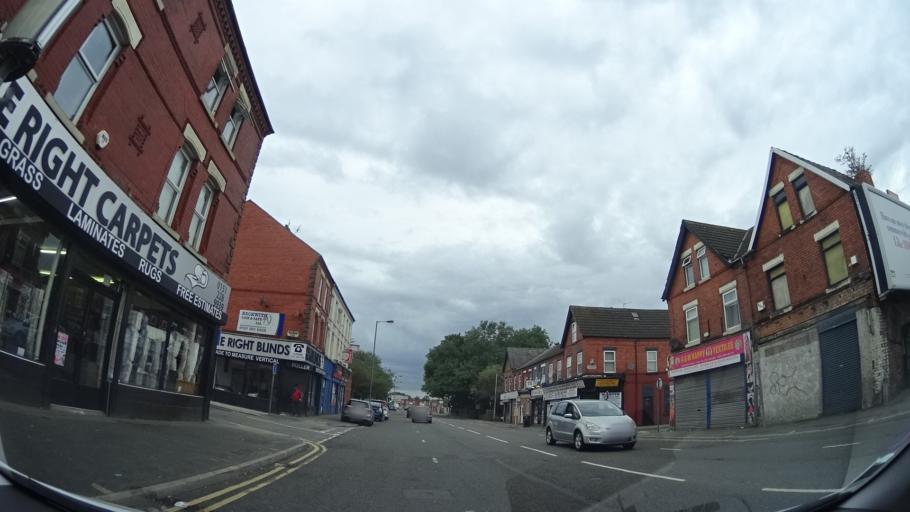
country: GB
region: England
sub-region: Liverpool
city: Liverpool
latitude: 53.4152
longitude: -2.9222
